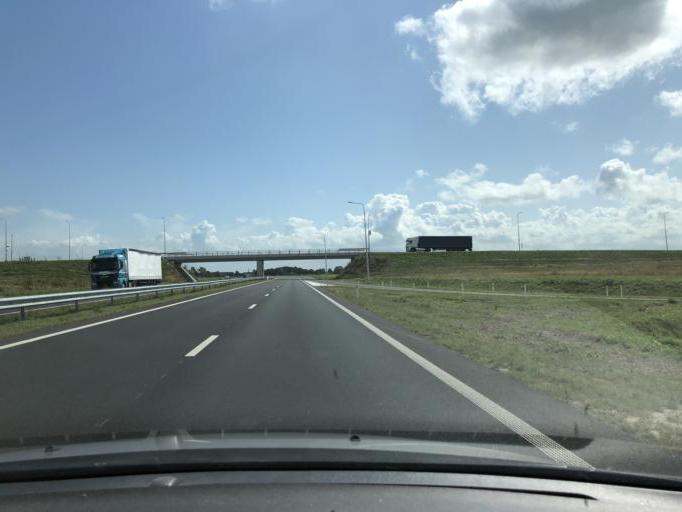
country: NL
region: North Holland
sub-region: Gemeente Medemblik
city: Medemblik
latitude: 52.6816
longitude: 5.1646
